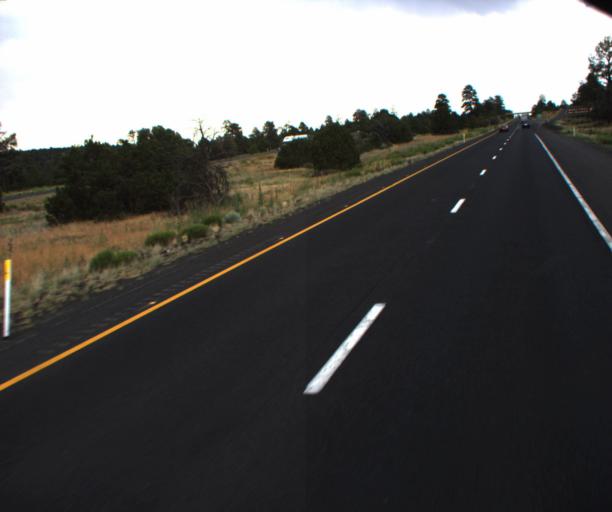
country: US
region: Arizona
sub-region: Coconino County
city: Flagstaff
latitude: 35.2101
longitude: -111.5248
